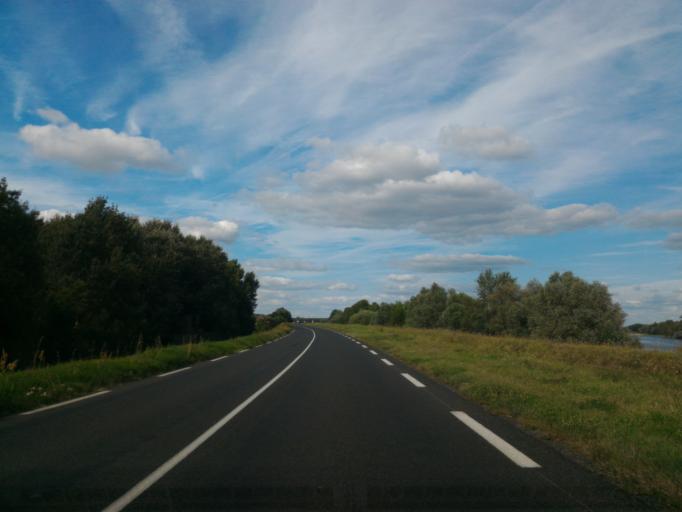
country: FR
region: Centre
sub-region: Departement d'Indre-et-Loire
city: Cangey
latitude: 47.4587
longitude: 1.0779
